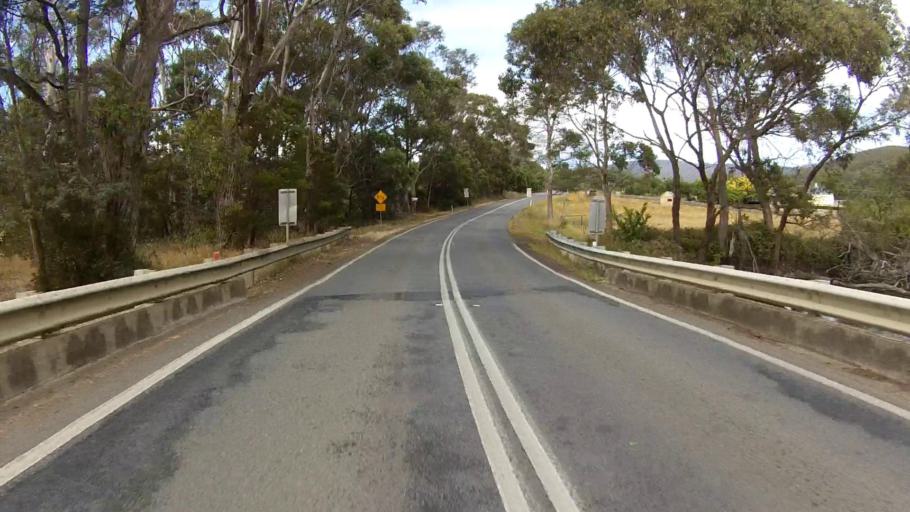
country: AU
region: Tasmania
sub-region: Kingborough
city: Kettering
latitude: -43.1336
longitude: 147.2517
